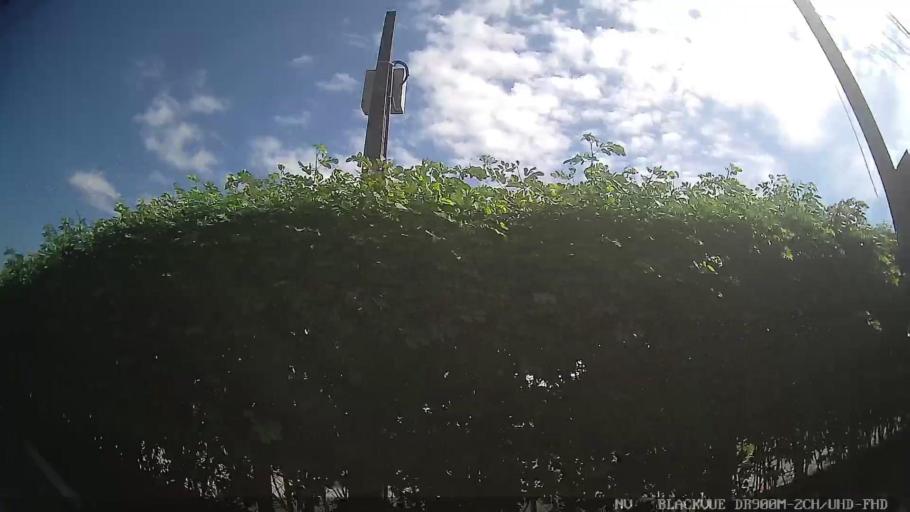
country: BR
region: Sao Paulo
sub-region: Jarinu
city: Jarinu
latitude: -23.0742
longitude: -46.6551
